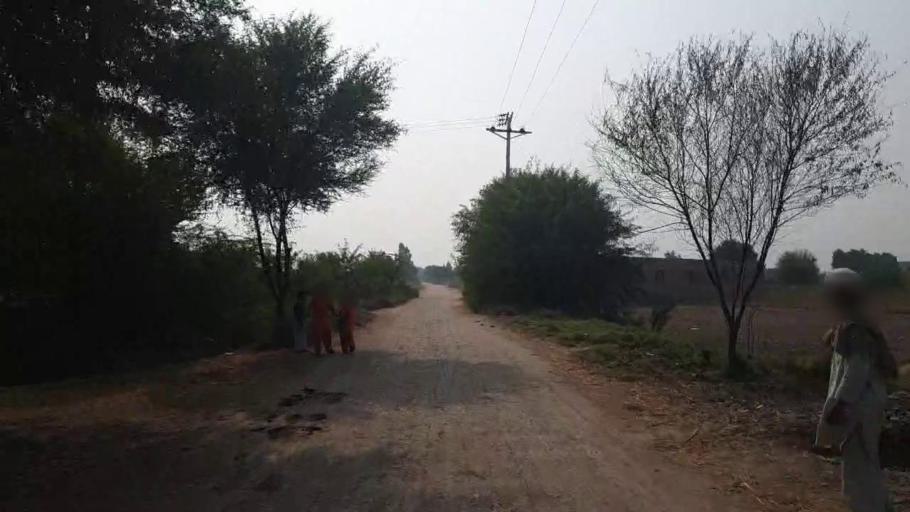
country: PK
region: Sindh
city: Tando Muhammad Khan
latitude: 25.2424
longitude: 68.5714
